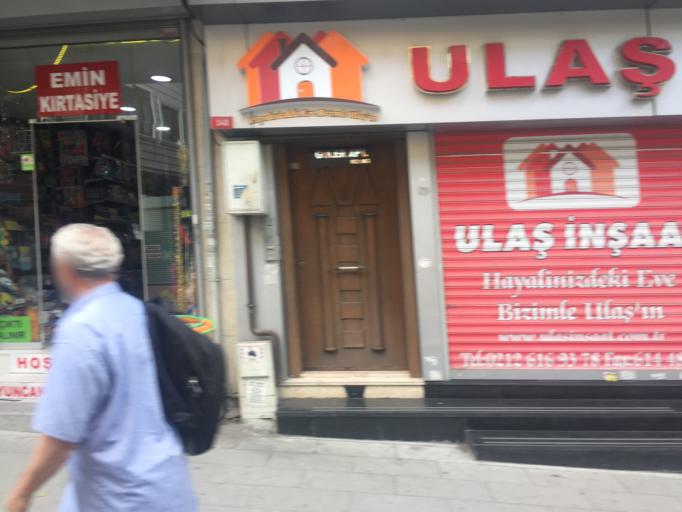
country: TR
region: Istanbul
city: Esenler
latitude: 41.0516
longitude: 28.9056
